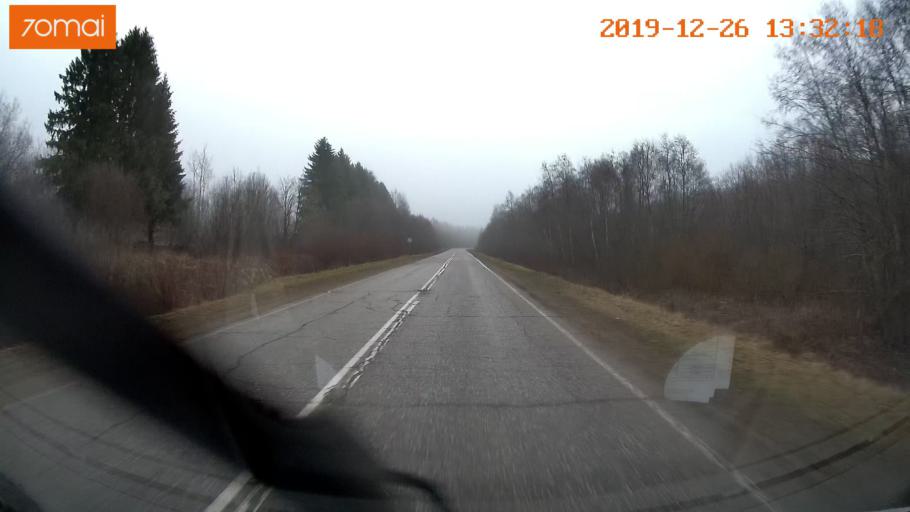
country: RU
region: Vologda
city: Sheksna
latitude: 58.8302
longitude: 38.2881
